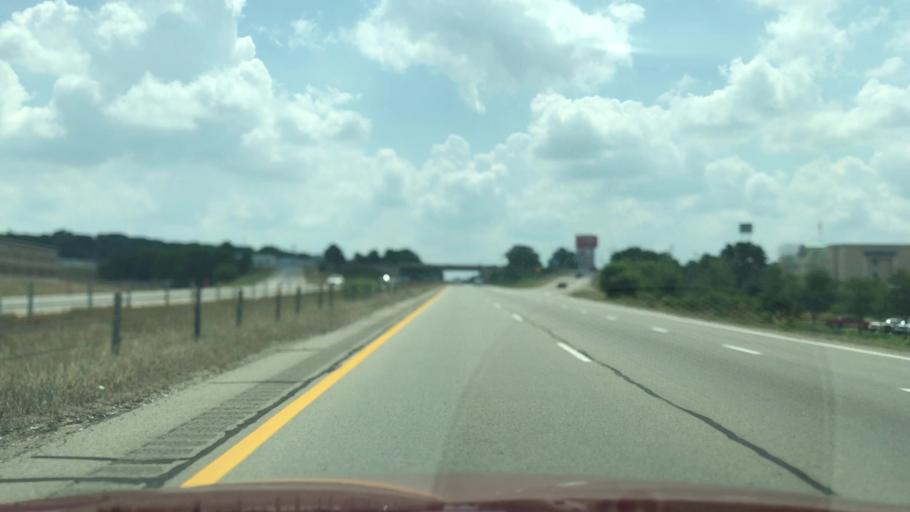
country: US
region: Michigan
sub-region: Kent County
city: Cutlerville
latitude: 42.8151
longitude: -85.6690
